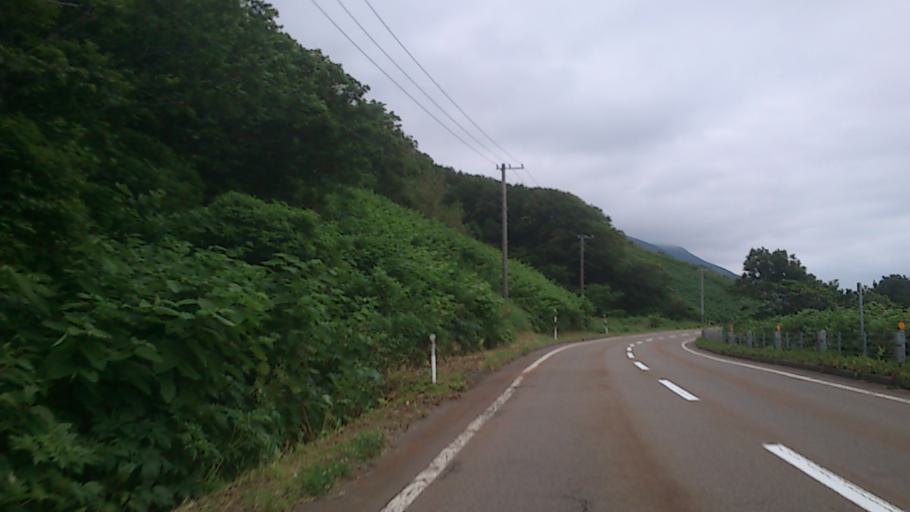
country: JP
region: Hokkaido
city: Kamiiso
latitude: 41.6701
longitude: 140.0060
